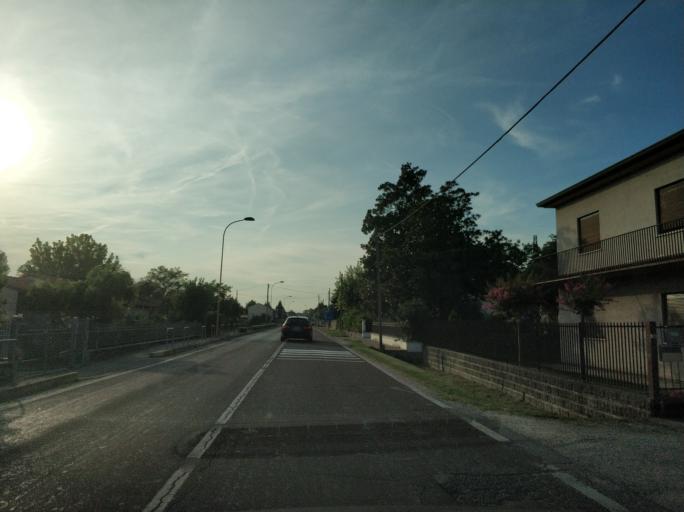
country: IT
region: Veneto
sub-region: Provincia di Padova
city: Este
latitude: 45.2148
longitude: 11.6706
